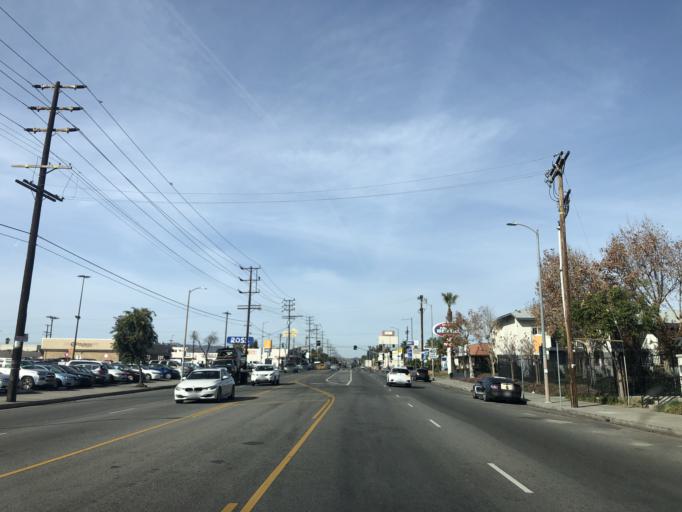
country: US
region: California
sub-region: Los Angeles County
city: San Fernando
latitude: 34.2457
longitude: -118.4183
